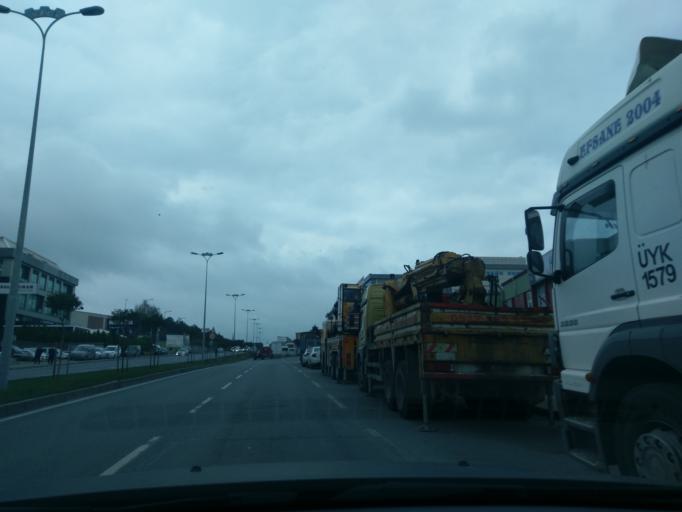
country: TR
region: Istanbul
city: Basaksehir
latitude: 41.0748
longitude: 28.7998
